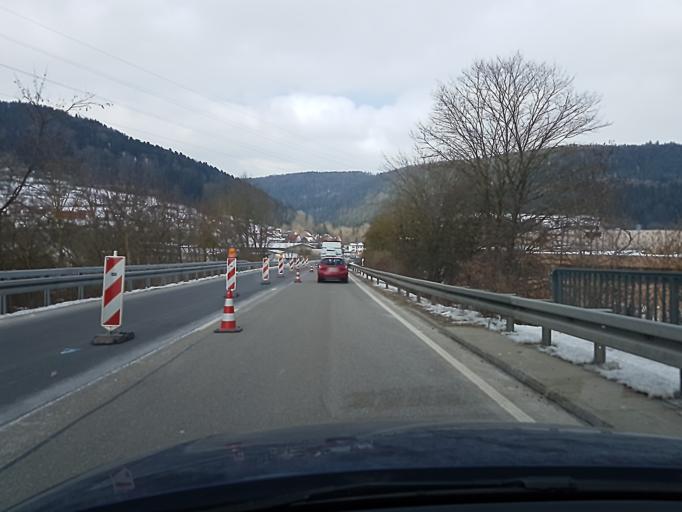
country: DE
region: Baden-Wuerttemberg
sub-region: Freiburg Region
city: Sulz am Neckar
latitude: 48.4174
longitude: 8.6372
